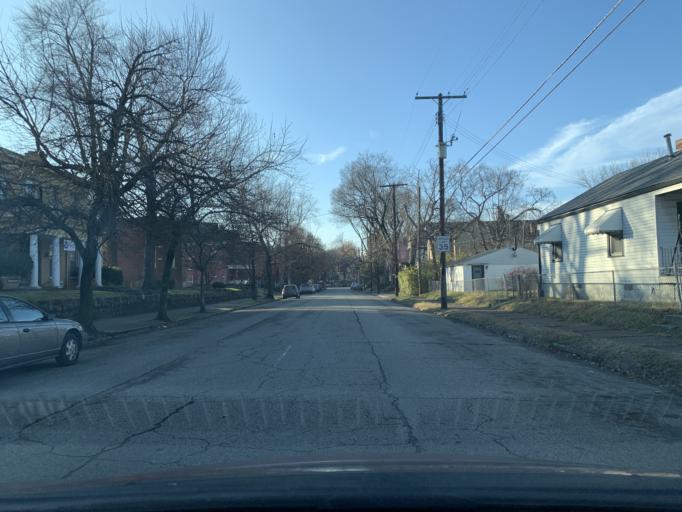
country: US
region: Kentucky
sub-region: Jefferson County
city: Louisville
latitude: 38.2293
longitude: -85.7526
